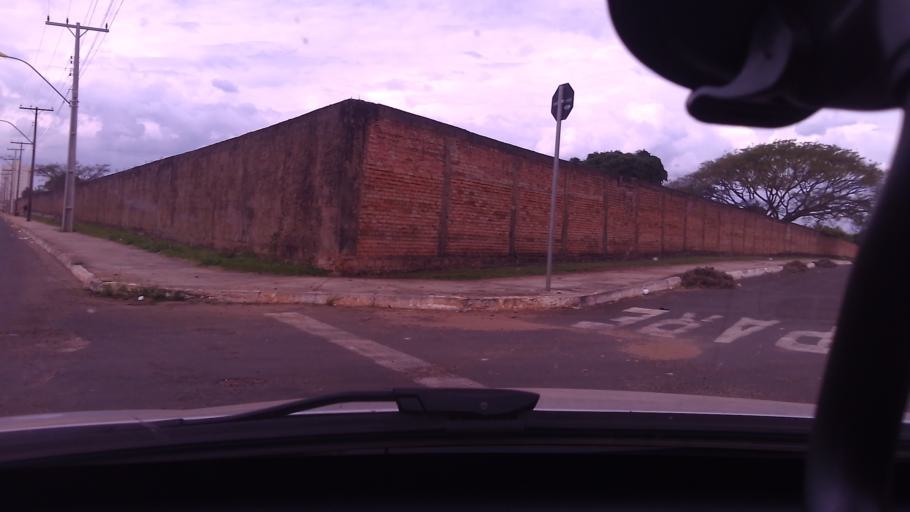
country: BR
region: Goias
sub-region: Mineiros
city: Mineiros
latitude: -17.5670
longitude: -52.5708
